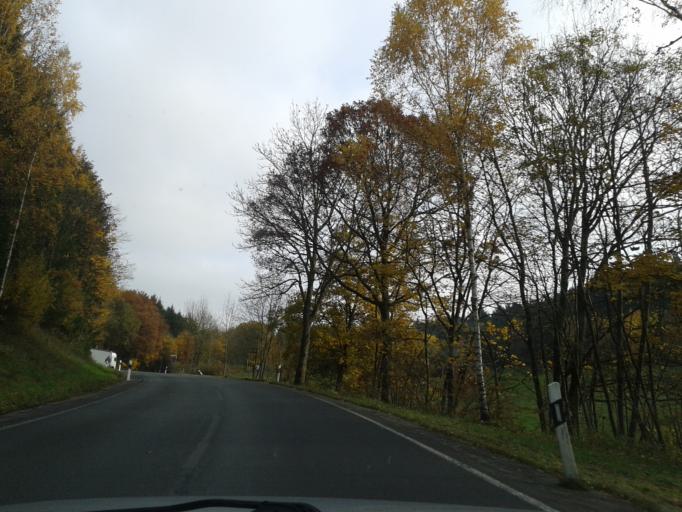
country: DE
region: North Rhine-Westphalia
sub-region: Regierungsbezirk Arnsberg
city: Bad Laasphe
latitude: 50.8662
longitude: 8.3646
